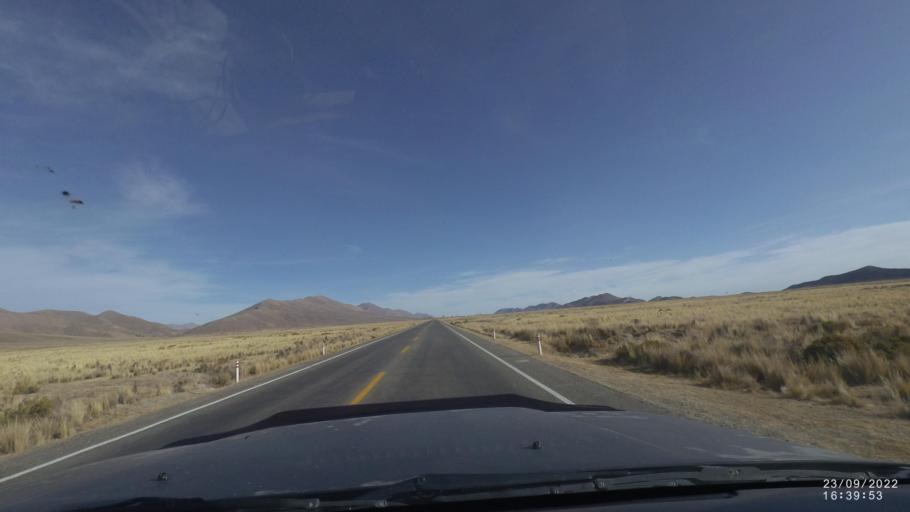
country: BO
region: Oruro
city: Machacamarca
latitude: -18.2669
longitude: -66.9981
